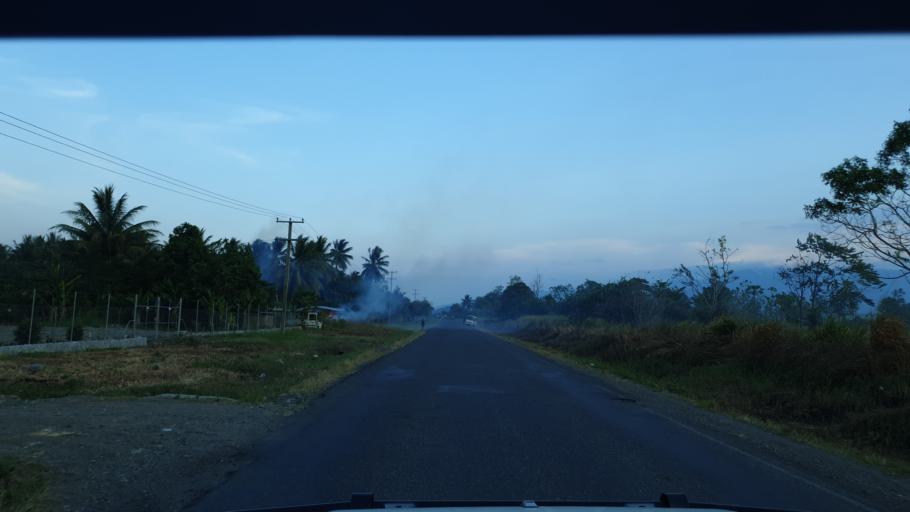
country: PG
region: Morobe
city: Lae
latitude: -6.5901
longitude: 146.7784
